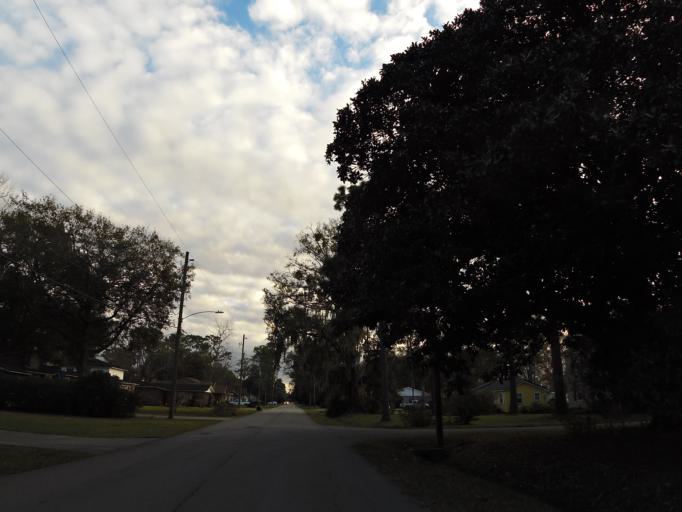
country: US
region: Florida
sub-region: Duval County
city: Jacksonville
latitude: 30.3022
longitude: -81.7263
